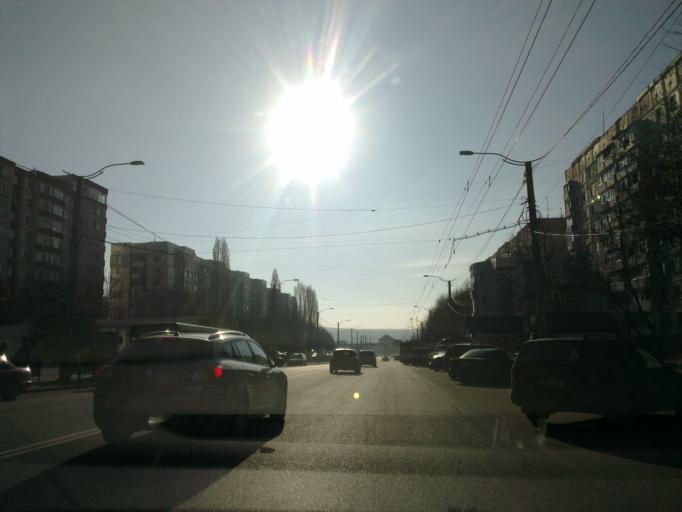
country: MD
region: Chisinau
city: Chisinau
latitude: 47.0386
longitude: 28.8840
